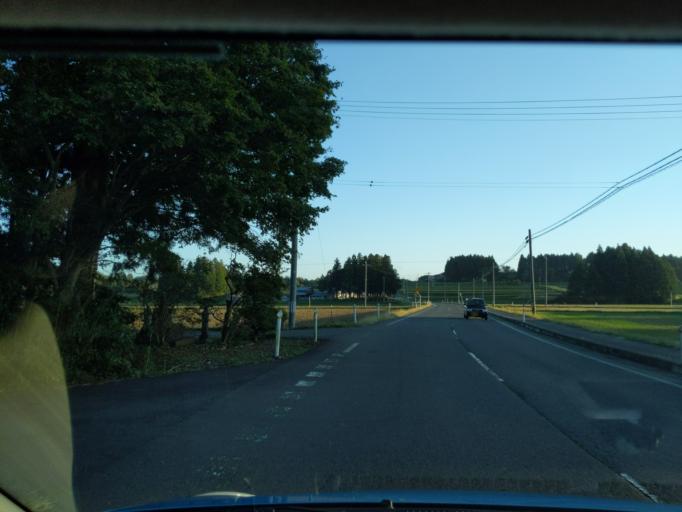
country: JP
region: Iwate
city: Mizusawa
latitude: 39.0762
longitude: 141.0935
